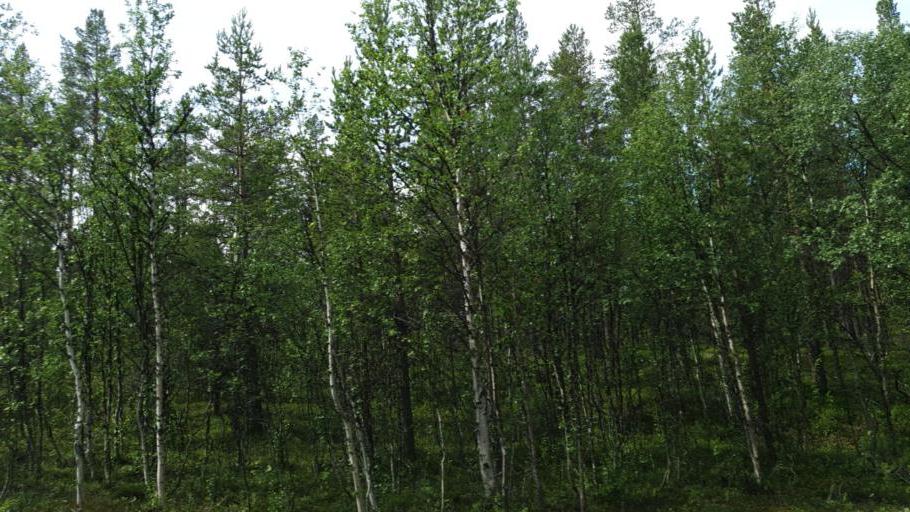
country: NO
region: Oppland
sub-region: Vaga
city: Vagamo
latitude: 61.7033
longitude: 9.0584
